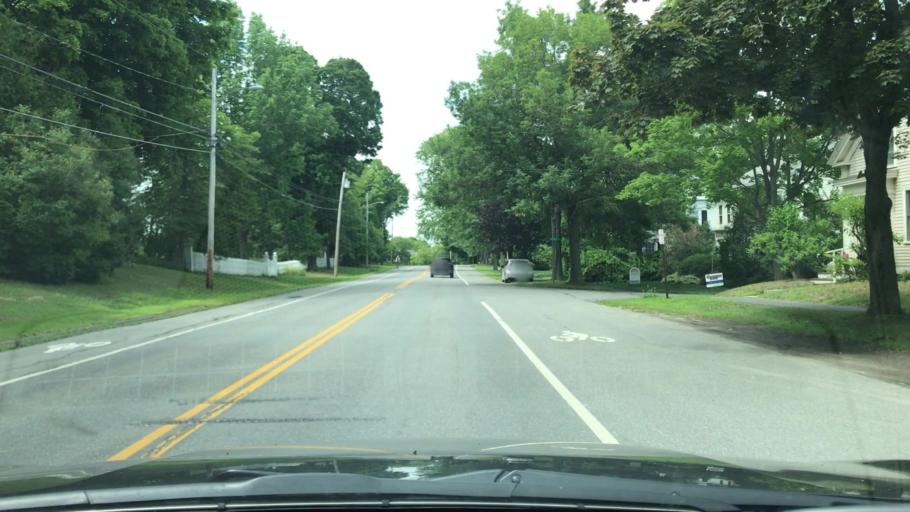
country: US
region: Maine
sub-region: Waldo County
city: Belfast
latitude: 44.4211
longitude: -69.0000
